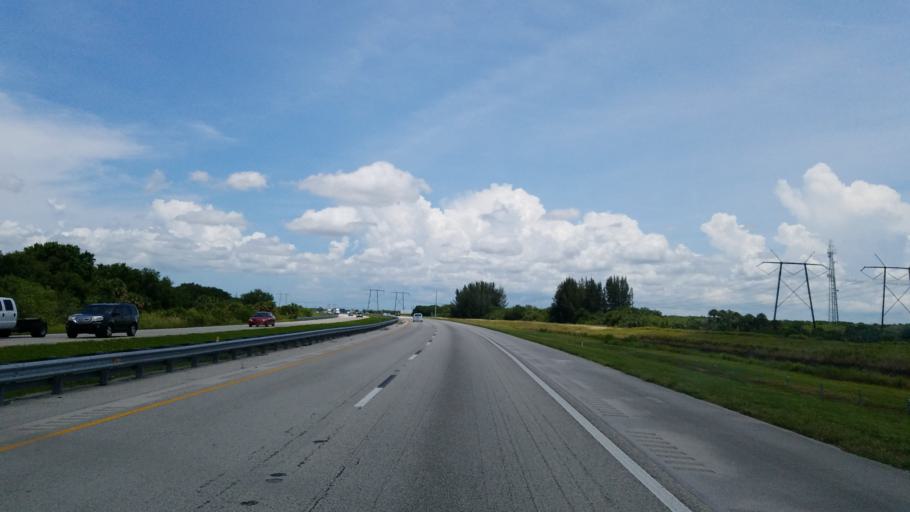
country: US
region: Florida
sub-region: Indian River County
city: West Vero Corridor
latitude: 27.4887
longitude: -80.5701
